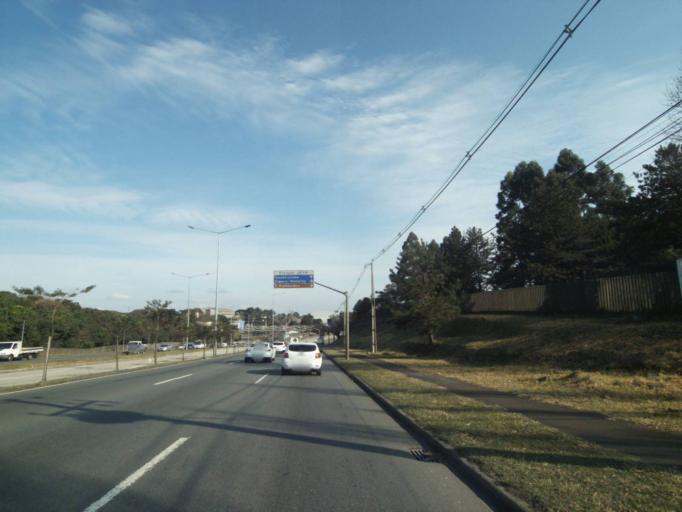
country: BR
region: Parana
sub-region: Curitiba
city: Curitiba
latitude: -25.4465
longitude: -49.2349
